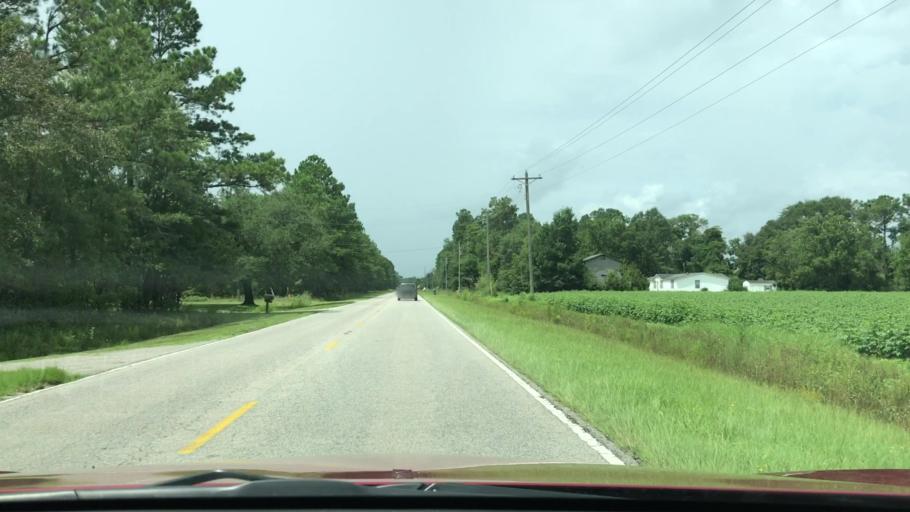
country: US
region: South Carolina
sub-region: Horry County
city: Red Hill
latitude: 33.8952
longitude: -78.9390
